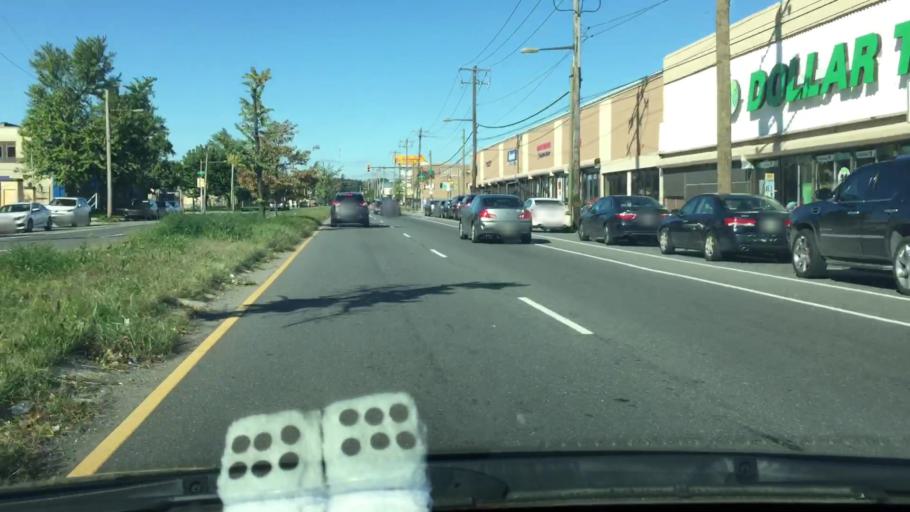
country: US
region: Pennsylvania
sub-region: Philadelphia County
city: Philadelphia
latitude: 39.9182
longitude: -75.1814
